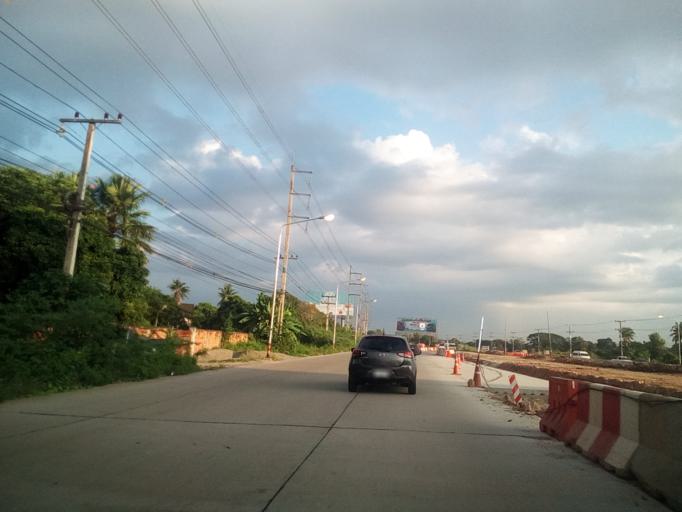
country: TH
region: Chiang Mai
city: Saraphi
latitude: 18.6947
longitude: 99.0491
